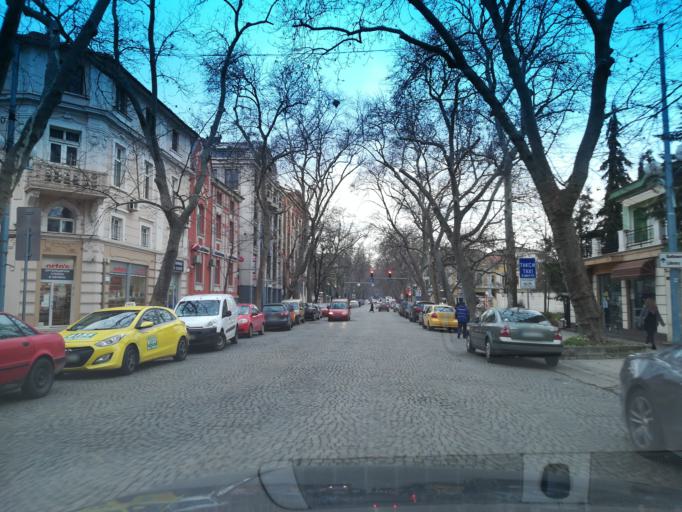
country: BG
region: Plovdiv
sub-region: Obshtina Plovdiv
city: Plovdiv
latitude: 42.1396
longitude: 24.7471
